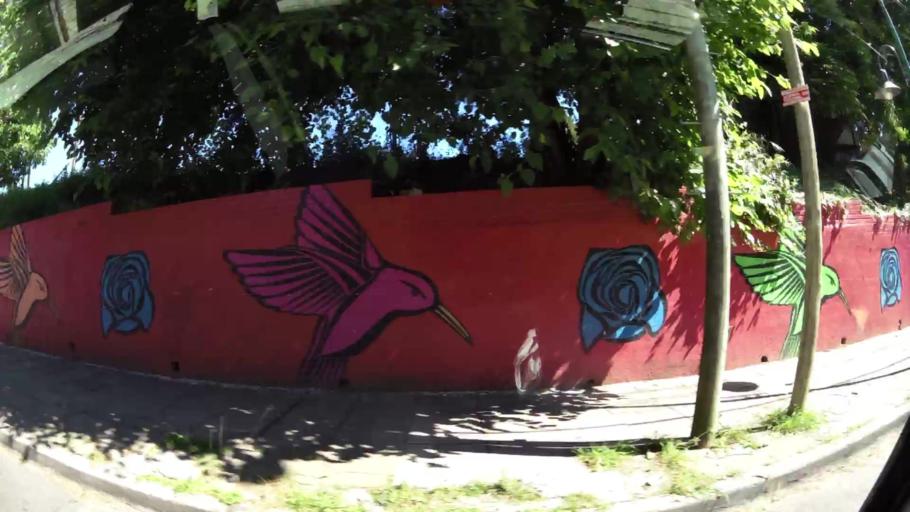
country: AR
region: Buenos Aires
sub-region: Partido de Vicente Lopez
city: Olivos
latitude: -34.5212
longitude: -58.4781
